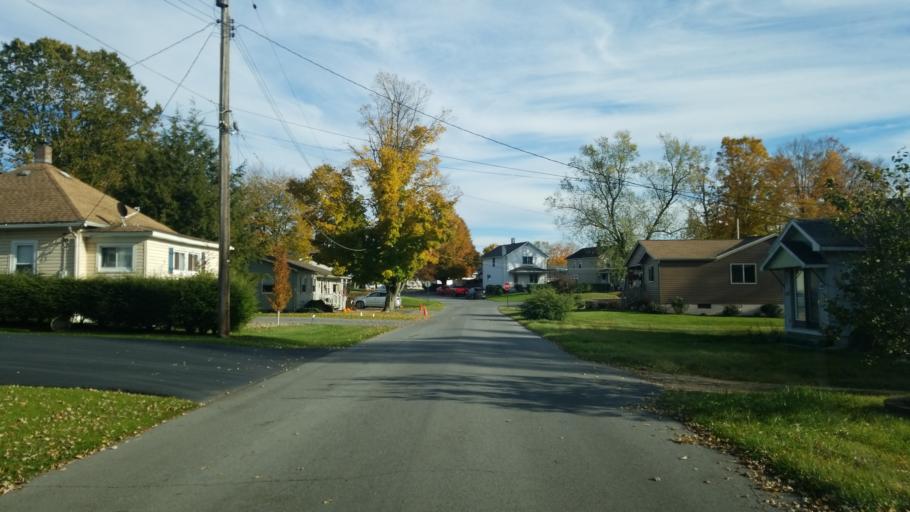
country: US
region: Pennsylvania
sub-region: Jefferson County
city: Brockway
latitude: 41.2486
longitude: -78.7859
